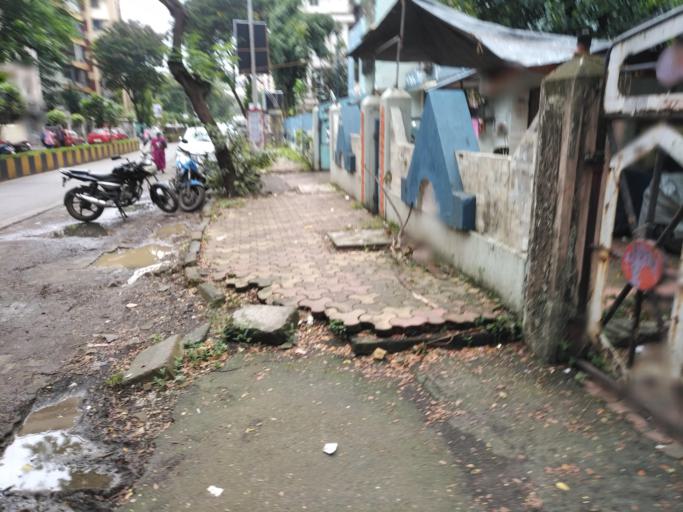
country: IN
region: Maharashtra
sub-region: Mumbai Suburban
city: Borivli
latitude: 19.2411
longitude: 72.8649
